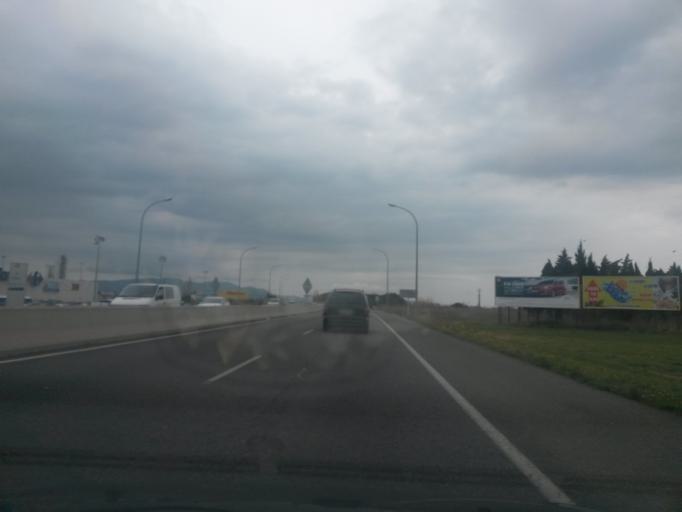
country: ES
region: Catalonia
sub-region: Provincia de Girona
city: Vila-sacra
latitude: 42.2675
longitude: 3.0005
